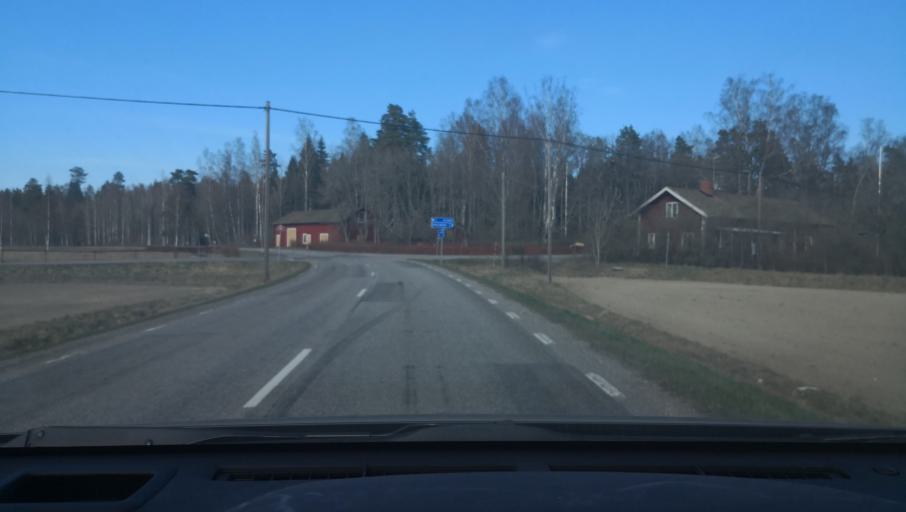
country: SE
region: Uppsala
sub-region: Heby Kommun
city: Heby
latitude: 59.9643
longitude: 16.8934
